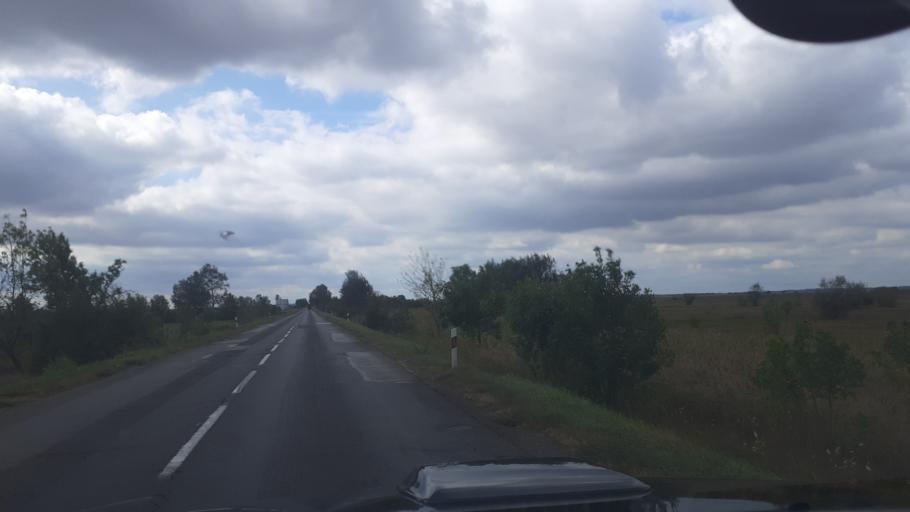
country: HU
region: Bacs-Kiskun
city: Fulopszallas
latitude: 46.8314
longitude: 19.2365
